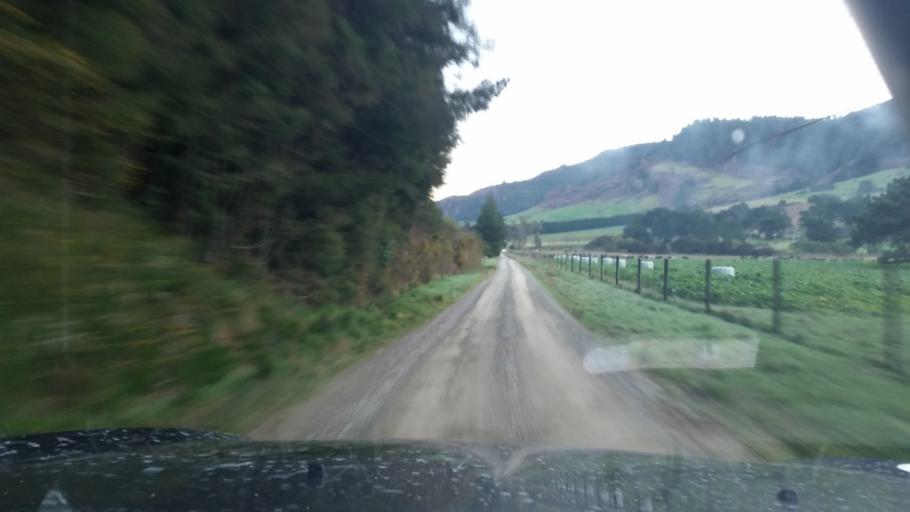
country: NZ
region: Marlborough
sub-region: Marlborough District
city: Picton
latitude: -41.1402
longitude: 174.1405
